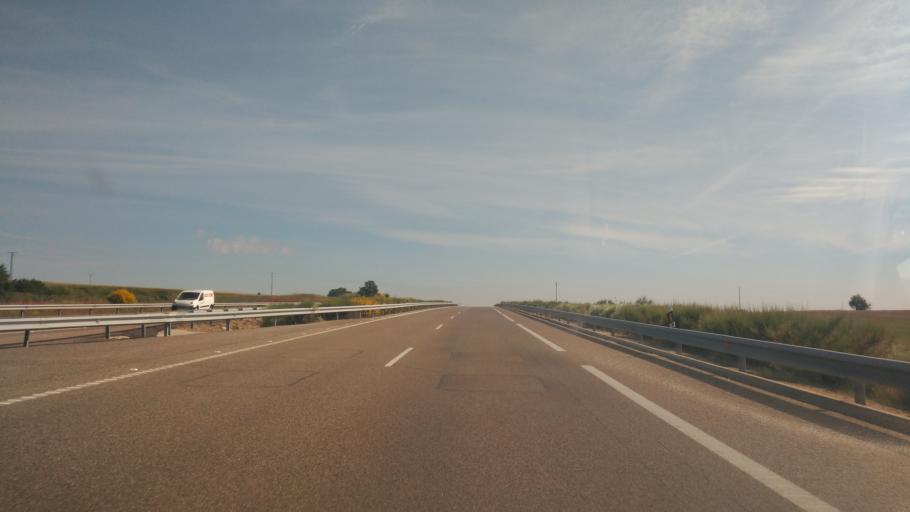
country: ES
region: Castille and Leon
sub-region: Provincia de Zamora
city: Corrales
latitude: 41.3824
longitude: -5.7185
